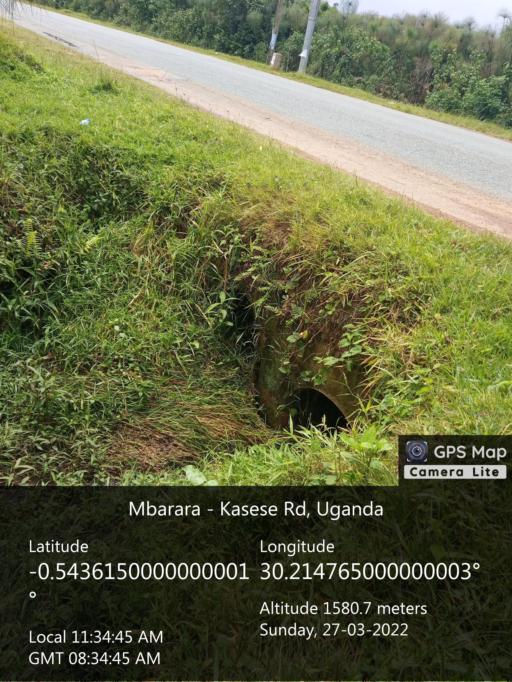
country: UG
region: Western Region
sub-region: Bushenyi District
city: Bushenyi
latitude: -0.5436
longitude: 30.2148
